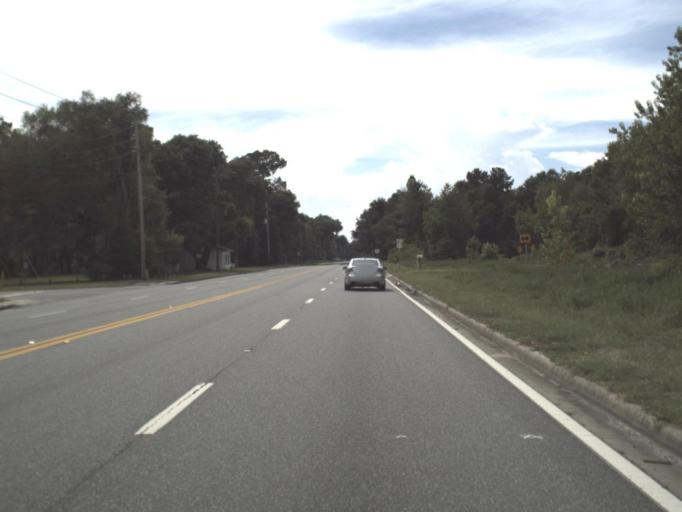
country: US
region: Florida
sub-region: Taylor County
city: Perry
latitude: 30.0912
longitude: -83.5371
